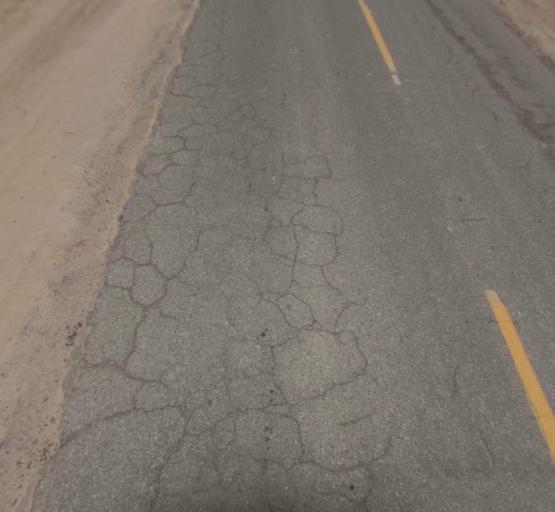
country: US
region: California
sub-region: Madera County
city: Parkwood
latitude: 36.8554
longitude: -120.1647
